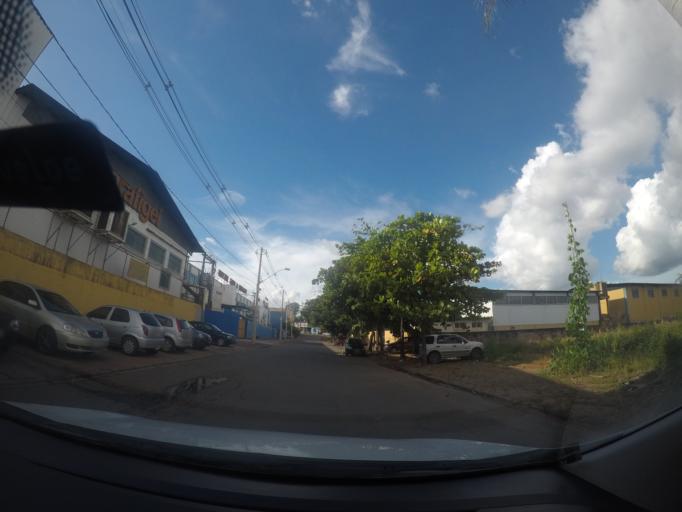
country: BR
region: Goias
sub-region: Goiania
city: Goiania
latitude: -16.6714
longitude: -49.2992
